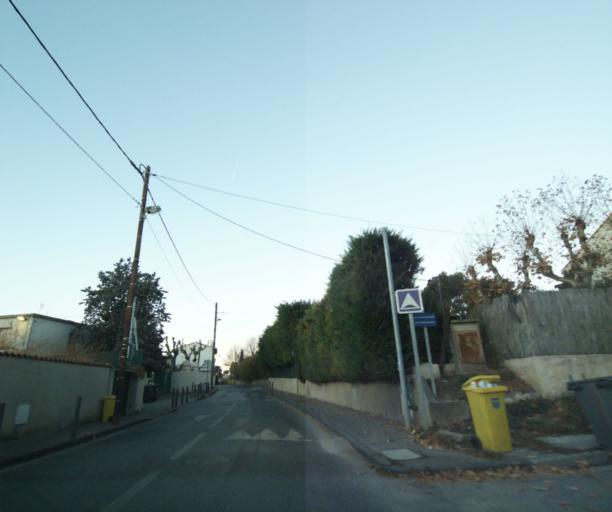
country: FR
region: Provence-Alpes-Cote d'Azur
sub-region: Departement des Bouches-du-Rhone
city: La Penne-sur-Huveaune
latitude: 43.3011
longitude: 5.5199
